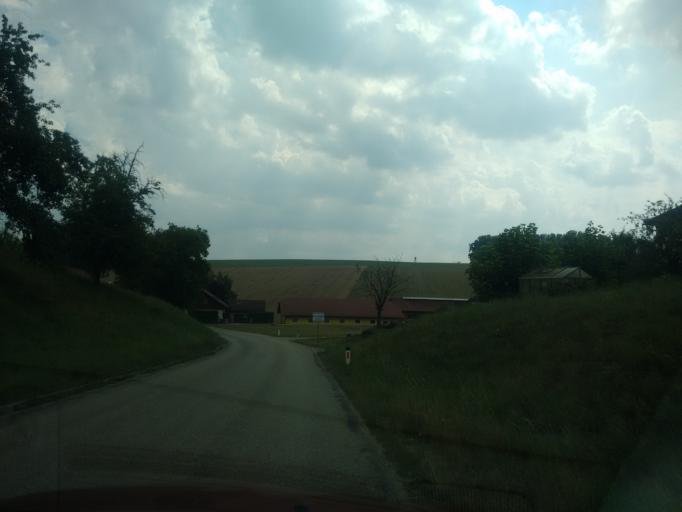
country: AT
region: Upper Austria
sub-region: Politischer Bezirk Grieskirchen
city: Bad Schallerbach
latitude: 48.2486
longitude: 13.9050
